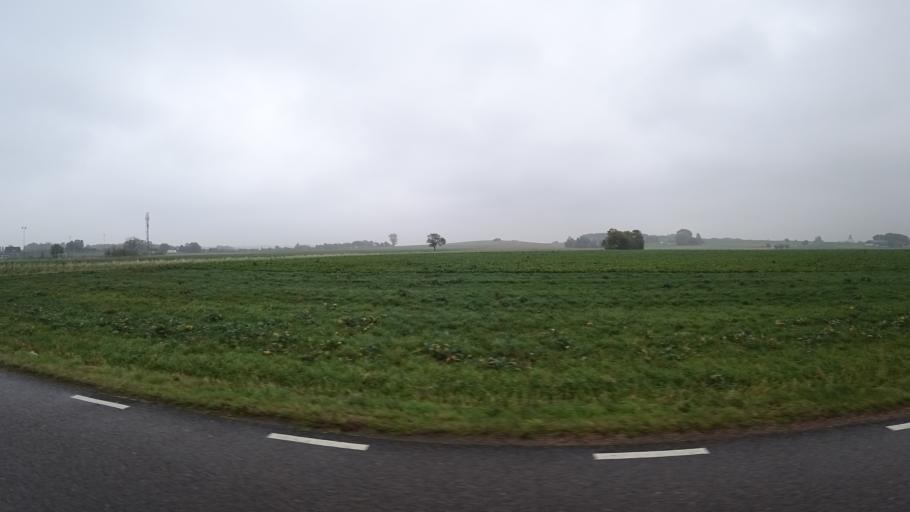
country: SE
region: Skane
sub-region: Kavlinge Kommun
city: Loddekopinge
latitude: 55.8161
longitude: 13.0257
